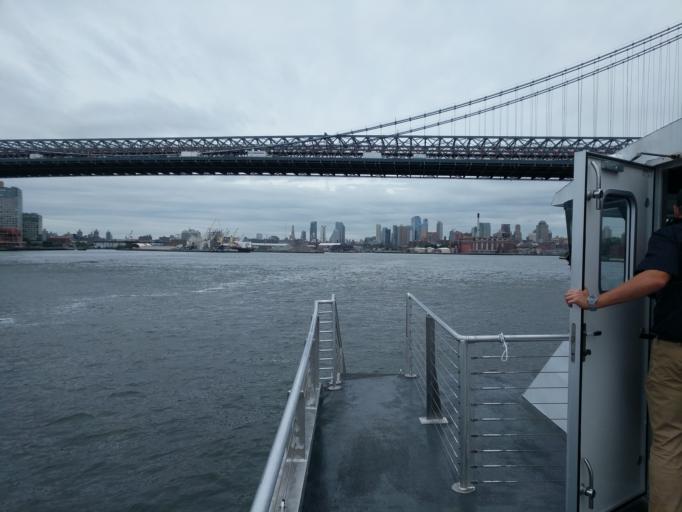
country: US
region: New York
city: New York City
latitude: 40.7158
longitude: -73.9726
